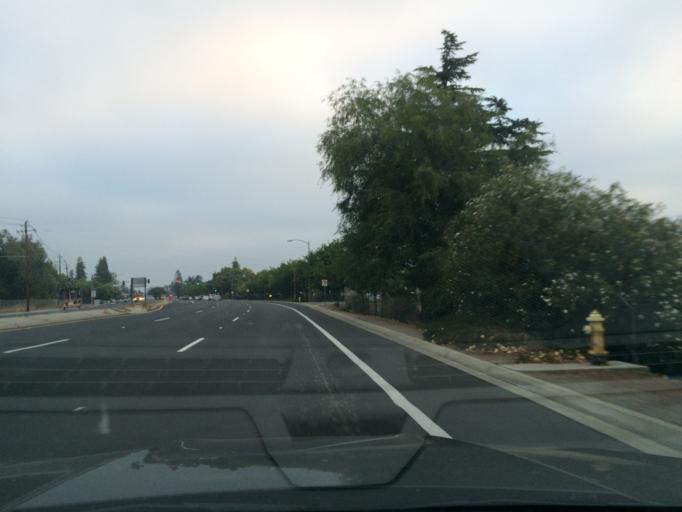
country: US
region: California
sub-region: Santa Clara County
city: Seven Trees
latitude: 37.2438
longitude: -121.8746
